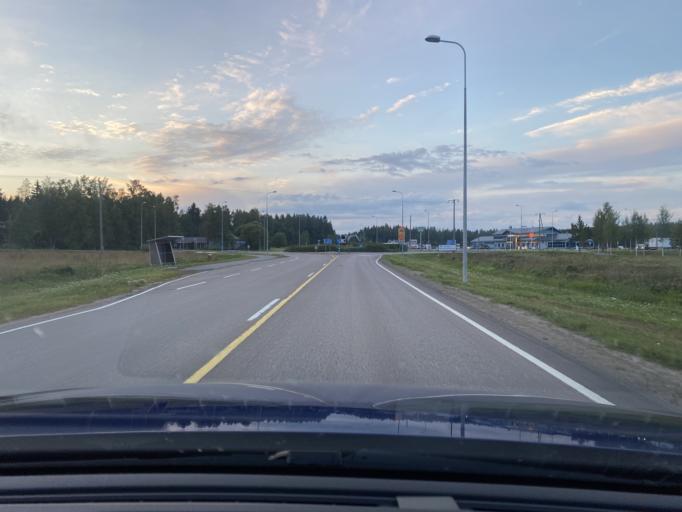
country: FI
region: Satakunta
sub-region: Pohjois-Satakunta
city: Honkajoki
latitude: 61.9904
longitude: 22.2415
